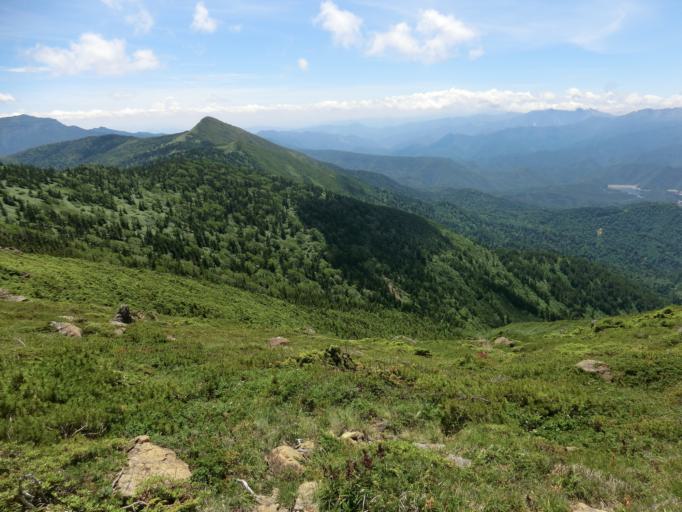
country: JP
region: Gunma
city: Numata
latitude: 36.8935
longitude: 139.1724
